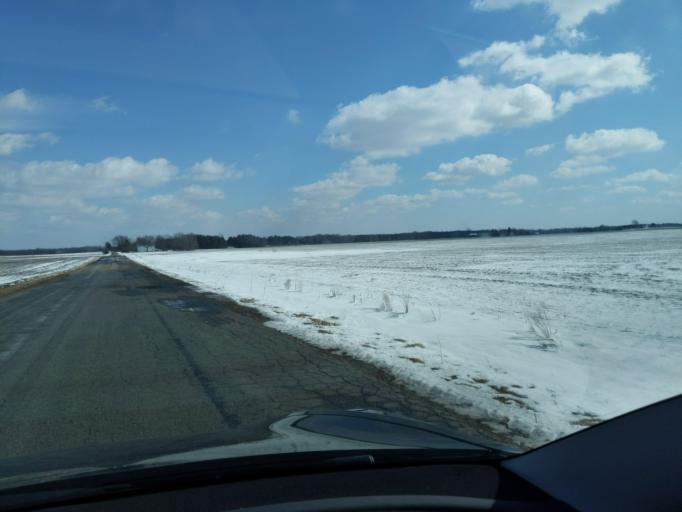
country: US
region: Michigan
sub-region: Ingham County
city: Williamston
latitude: 42.6155
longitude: -84.2887
